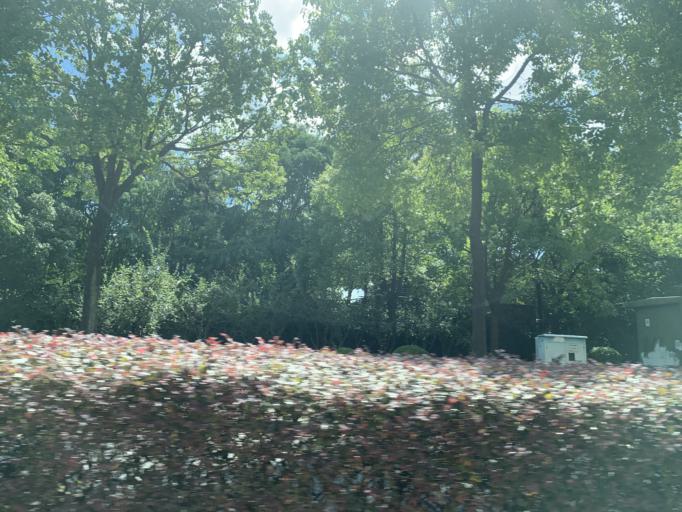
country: CN
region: Shanghai Shi
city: Huamu
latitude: 31.2332
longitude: 121.5793
